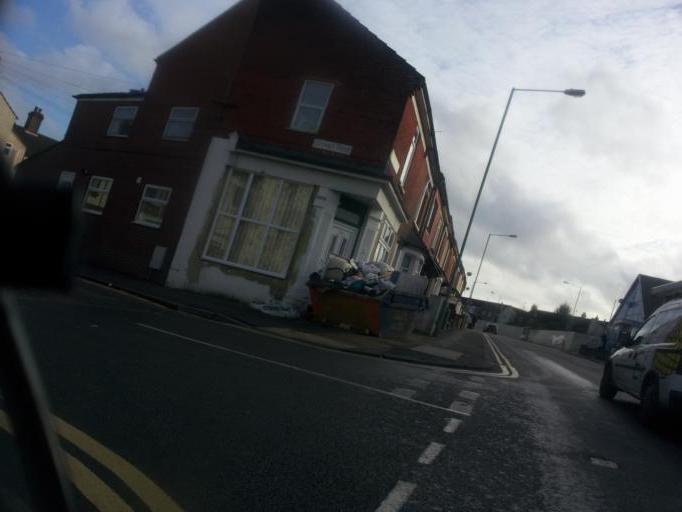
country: GB
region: England
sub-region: Kent
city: Gillingham
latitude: 51.3751
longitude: 0.5521
